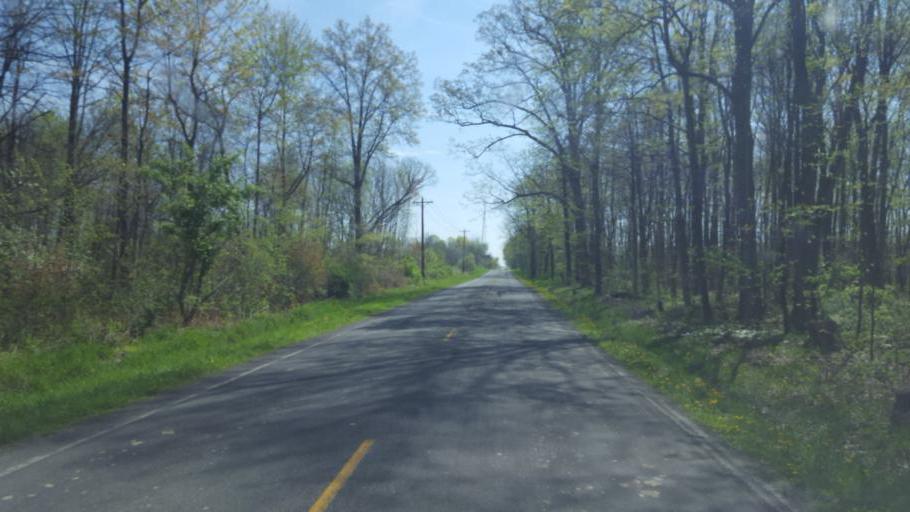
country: US
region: Ohio
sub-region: Wayne County
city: West Salem
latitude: 40.9915
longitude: -82.1048
